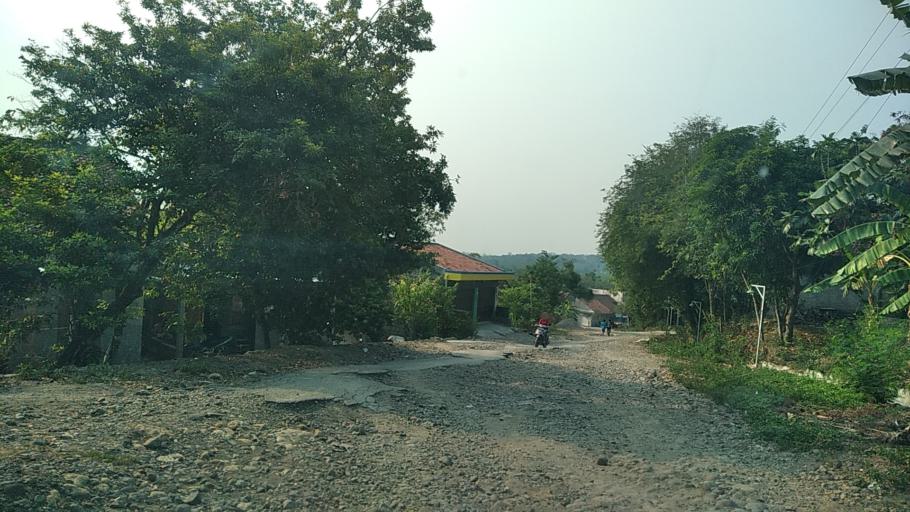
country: ID
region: Central Java
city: Mranggen
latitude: -7.0643
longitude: 110.4813
